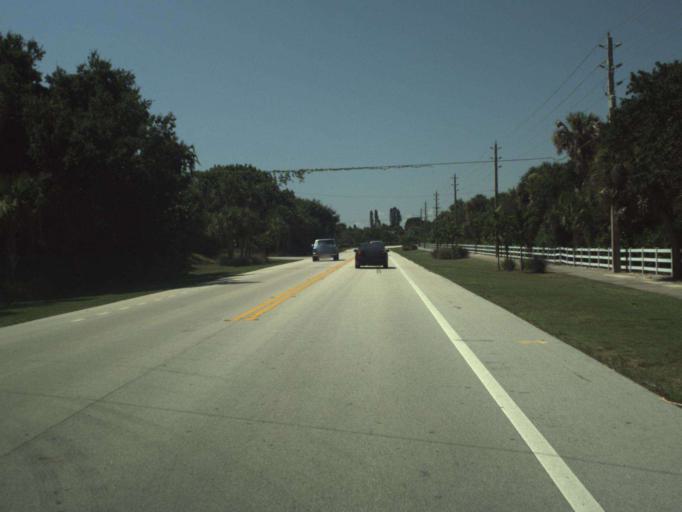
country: US
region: Florida
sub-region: Indian River County
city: South Beach
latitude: 27.5949
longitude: -80.3346
